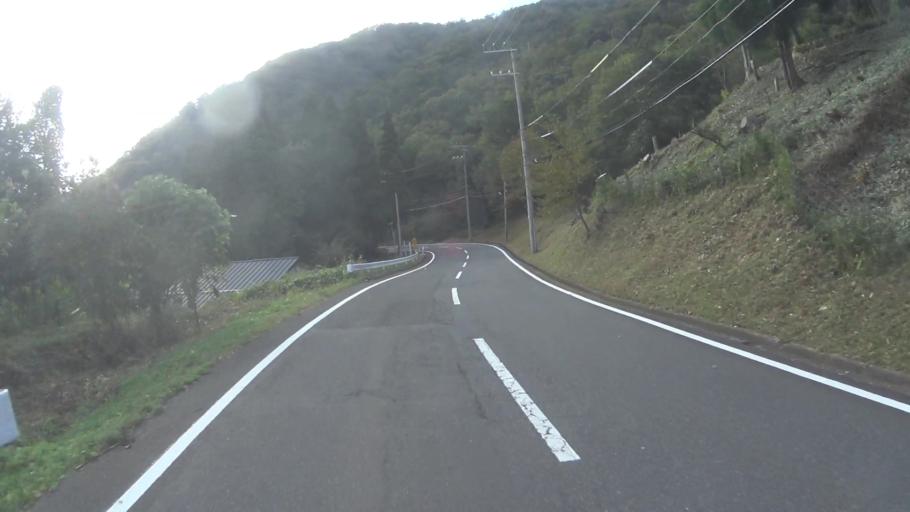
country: JP
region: Kyoto
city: Maizuru
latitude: 35.5339
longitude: 135.3947
